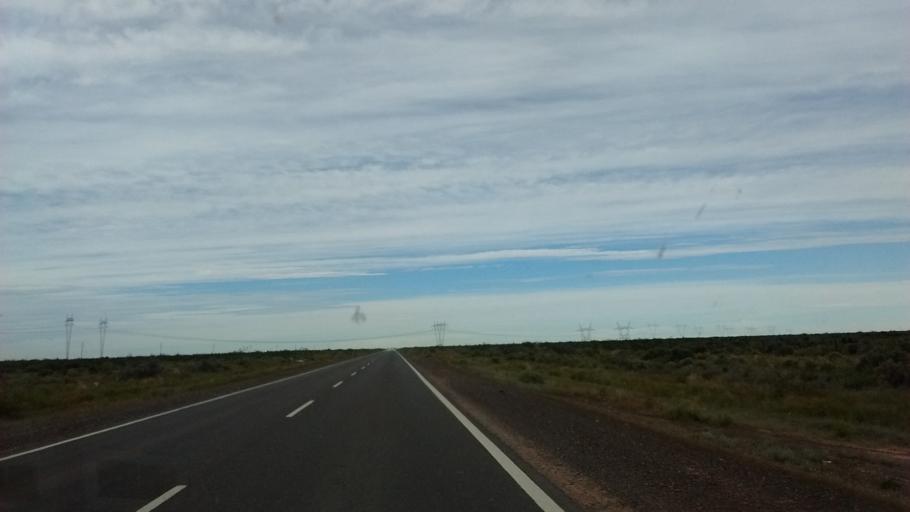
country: AR
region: Rio Negro
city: Contraalmirante Cordero
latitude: -38.5729
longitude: -68.0971
